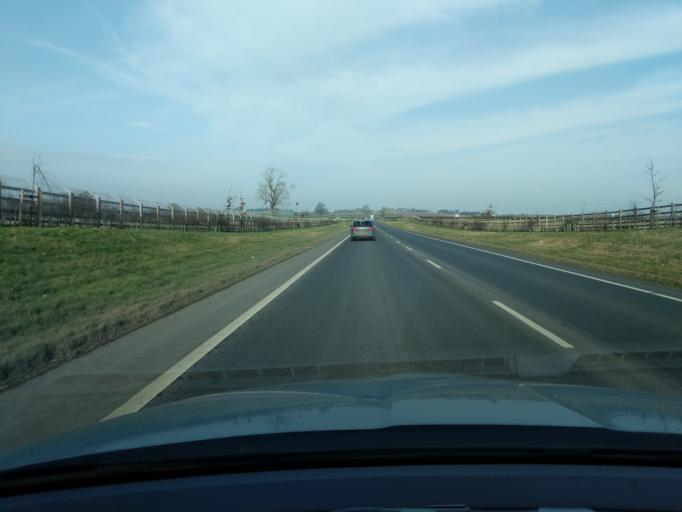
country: GB
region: England
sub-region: North Yorkshire
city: Bedale
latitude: 54.3023
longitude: -1.5855
